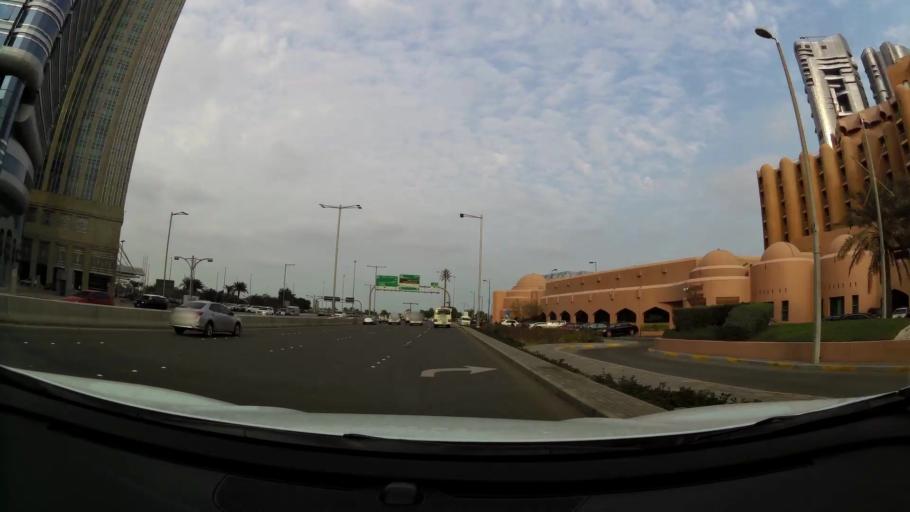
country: AE
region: Abu Dhabi
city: Abu Dhabi
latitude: 24.4999
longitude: 54.3684
